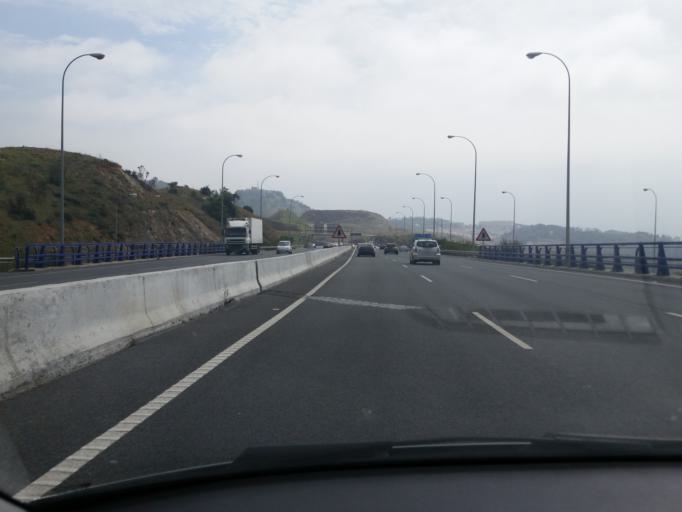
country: ES
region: Andalusia
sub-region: Provincia de Malaga
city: Malaga
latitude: 36.7432
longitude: -4.4054
